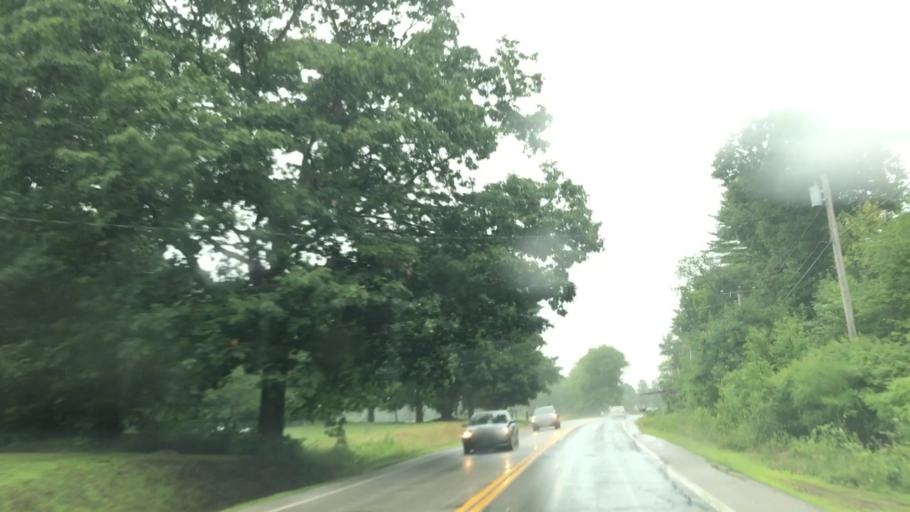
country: US
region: Maine
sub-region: York County
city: North Berwick
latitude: 43.2908
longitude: -70.7871
